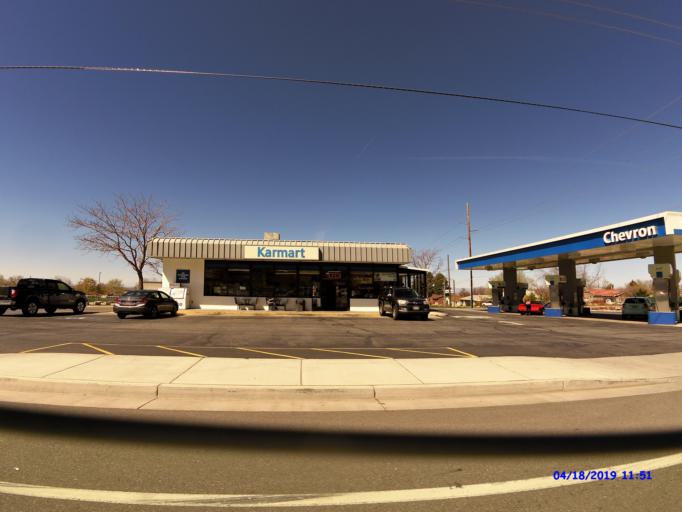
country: US
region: Utah
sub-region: Weber County
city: Ogden
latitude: 41.2587
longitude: -111.9479
